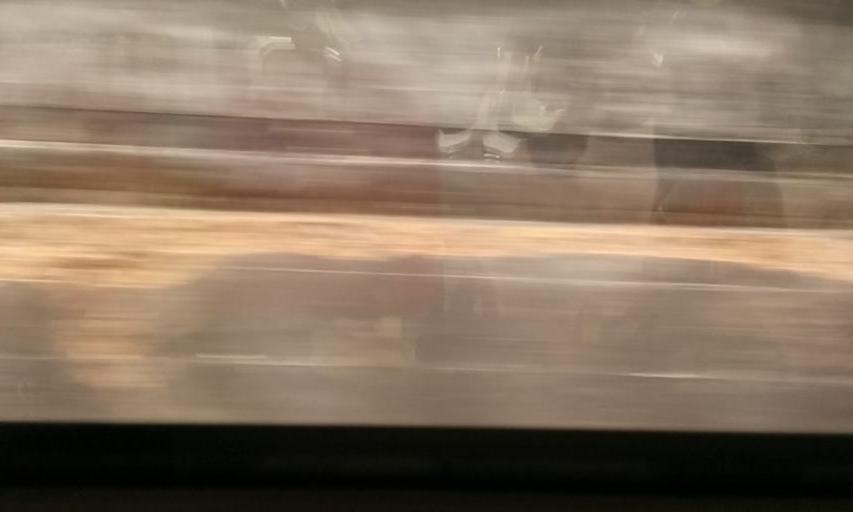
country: JP
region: Nagano
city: Ina
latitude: 35.7520
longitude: 137.7109
